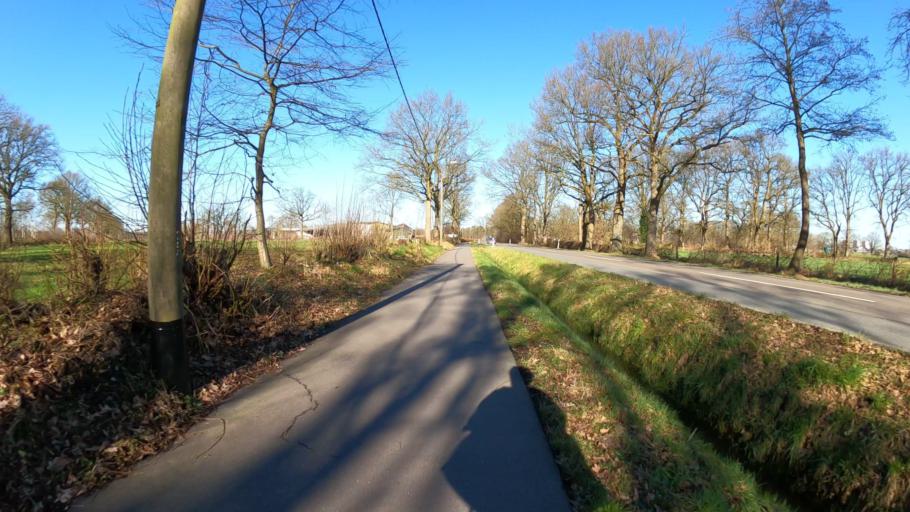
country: DE
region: Schleswig-Holstein
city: Rellingen
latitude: 53.6255
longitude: 9.7970
